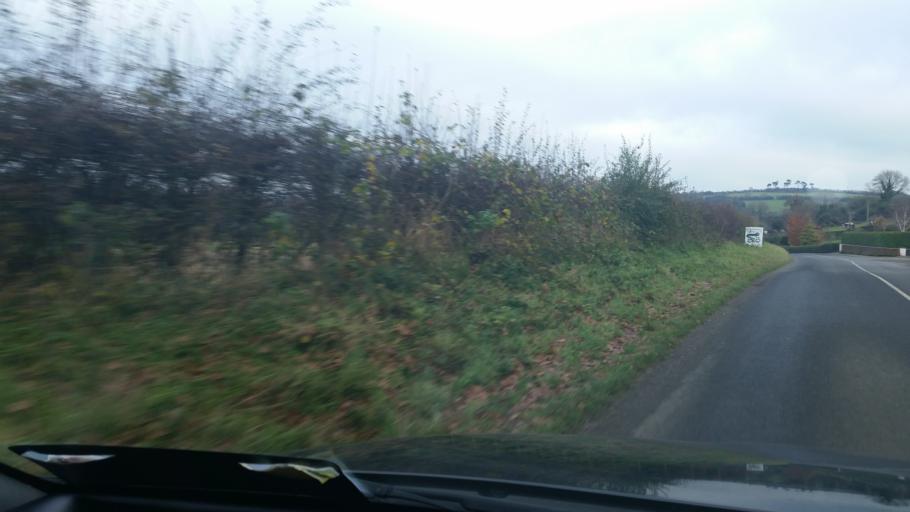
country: IE
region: Leinster
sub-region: An Mhi
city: Duleek
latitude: 53.6948
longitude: -6.4440
